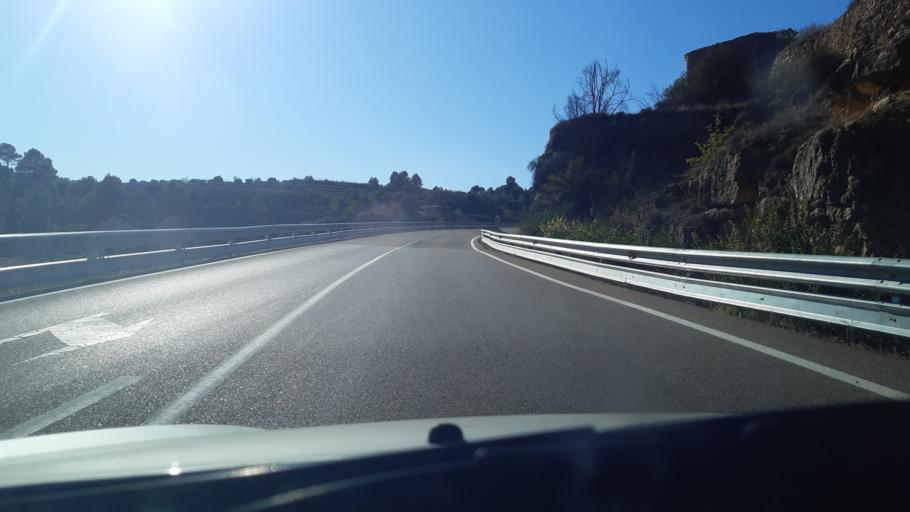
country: ES
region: Aragon
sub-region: Provincia de Teruel
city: Valjunquera
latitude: 40.9509
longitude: 0.0287
